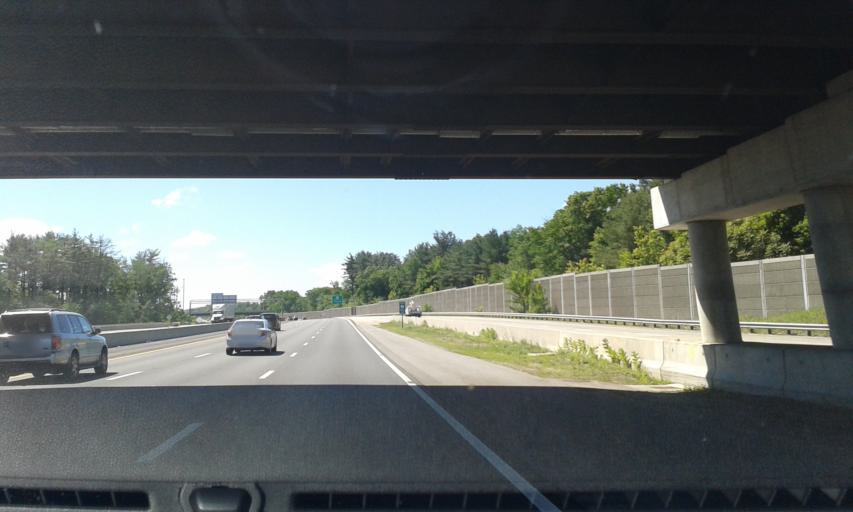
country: US
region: Massachusetts
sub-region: Middlesex County
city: Lowell
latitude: 42.6055
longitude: -71.3250
